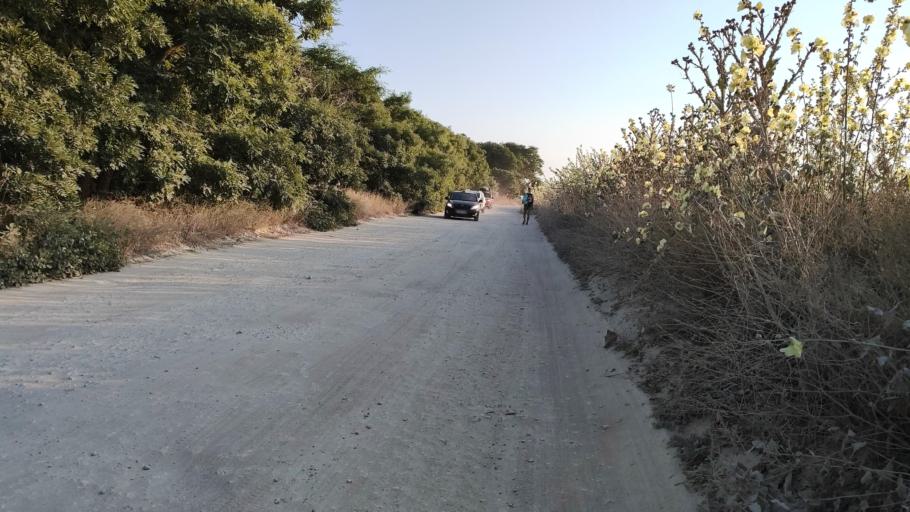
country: RU
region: Krasnodarskiy
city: Blagovetschenskaya
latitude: 45.0670
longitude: 37.0535
